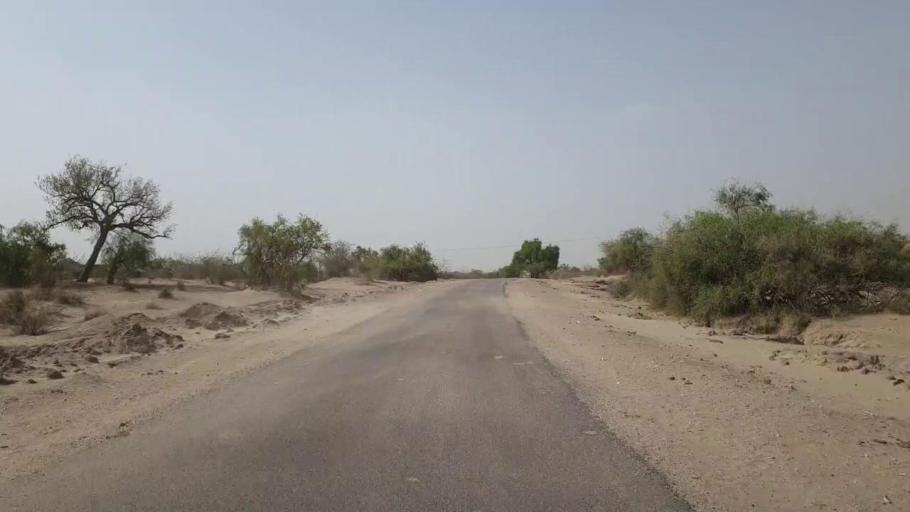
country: PK
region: Sindh
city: Mithi
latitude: 24.6097
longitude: 69.9206
